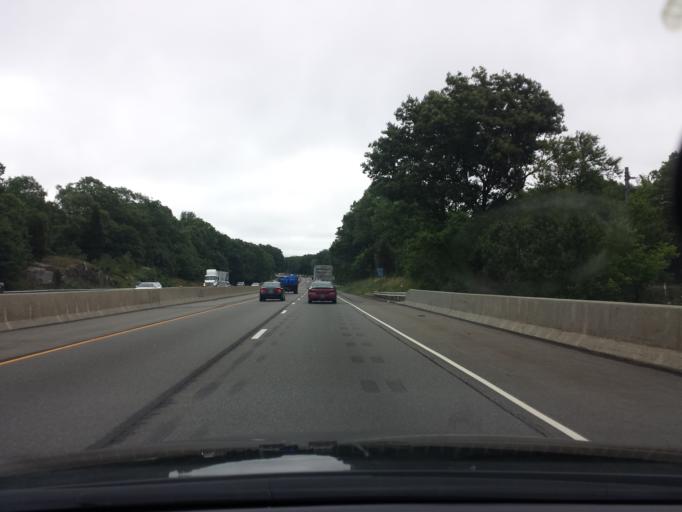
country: US
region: Connecticut
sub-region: New Haven County
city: Madison
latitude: 41.2899
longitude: -72.5647
